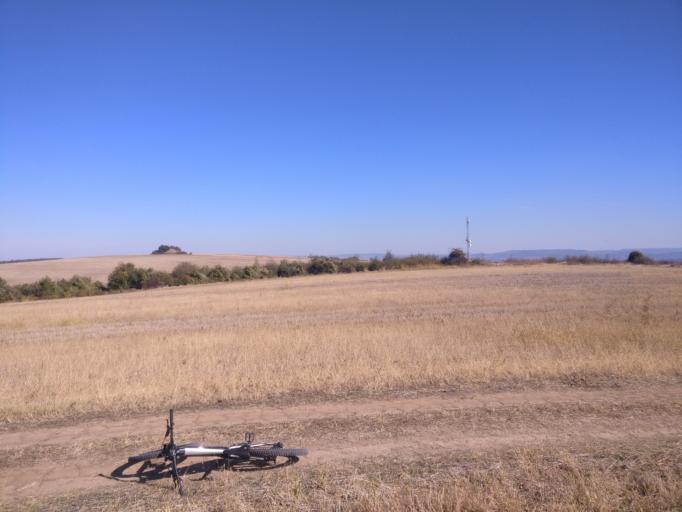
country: BG
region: Turgovishte
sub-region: Obshtina Opaka
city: Opaka
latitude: 43.3810
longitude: 26.0973
